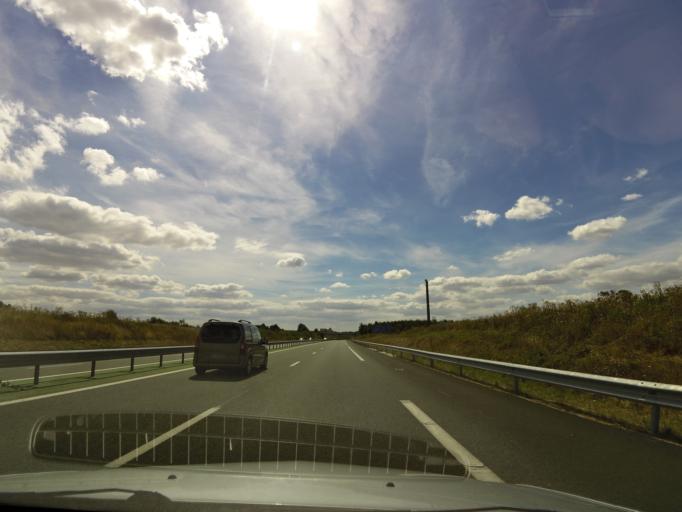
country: FR
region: Pays de la Loire
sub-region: Departement de la Vendee
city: Les Essarts
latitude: 46.7996
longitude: -1.2237
